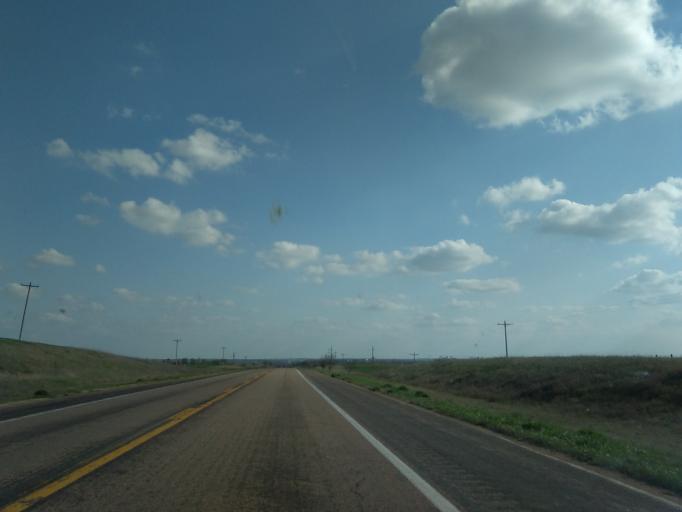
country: US
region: Nebraska
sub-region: Webster County
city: Red Cloud
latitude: 40.1225
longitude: -98.5190
